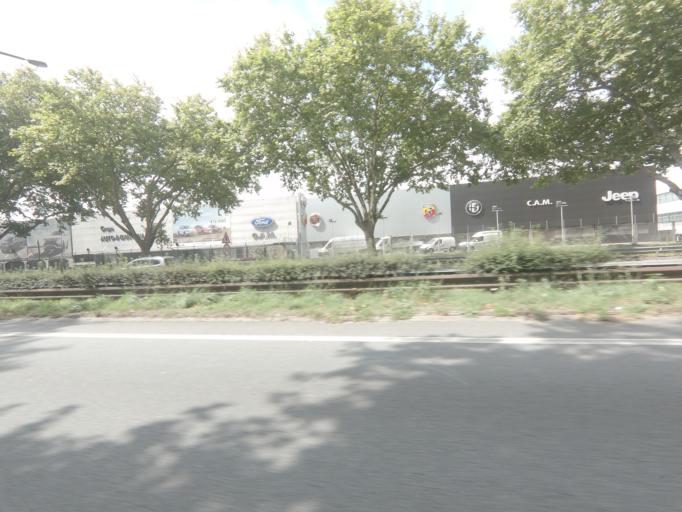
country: PT
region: Porto
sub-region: Matosinhos
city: Senhora da Hora
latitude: 41.1708
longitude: -8.6464
